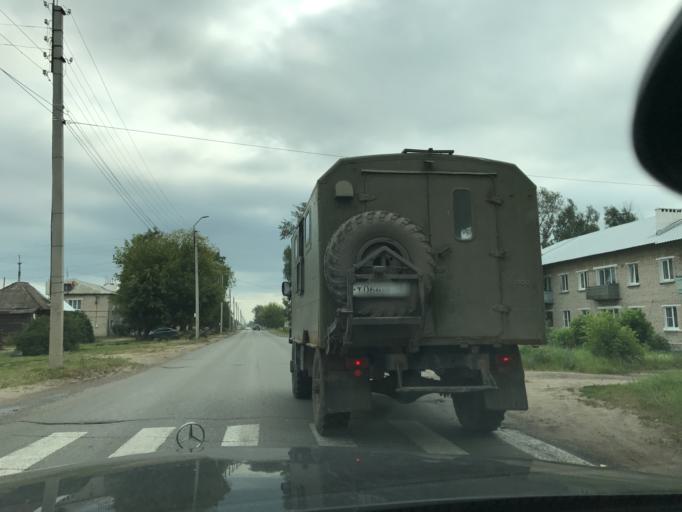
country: RU
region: Vladimir
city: Gorokhovets
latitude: 56.1956
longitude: 42.7083
